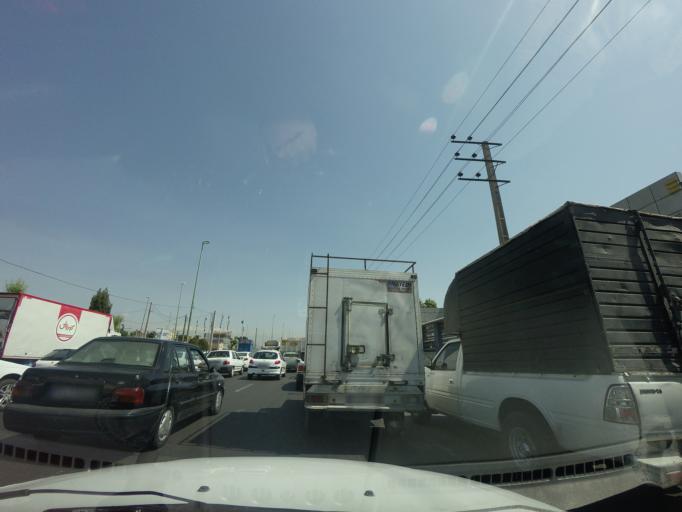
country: IR
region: Tehran
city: Eslamshahr
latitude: 35.5941
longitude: 51.2942
